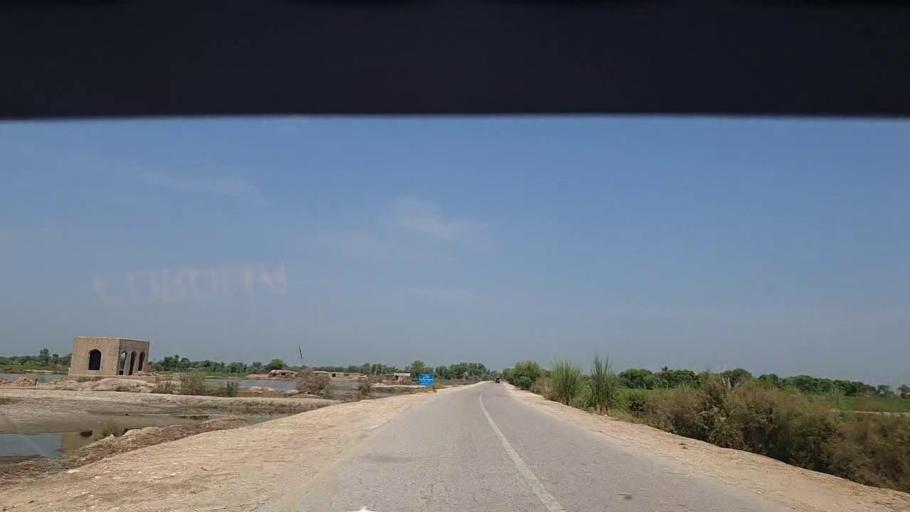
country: PK
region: Sindh
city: Thul
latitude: 28.1384
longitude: 68.8175
